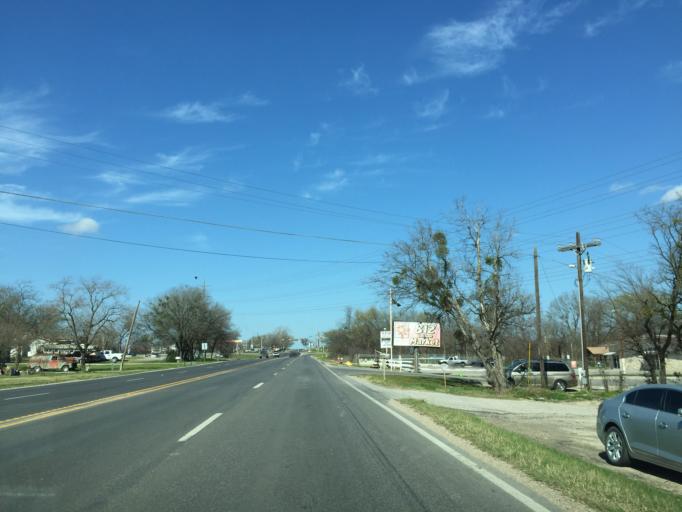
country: US
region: Texas
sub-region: Travis County
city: Onion Creek
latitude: 30.1631
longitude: -97.6904
